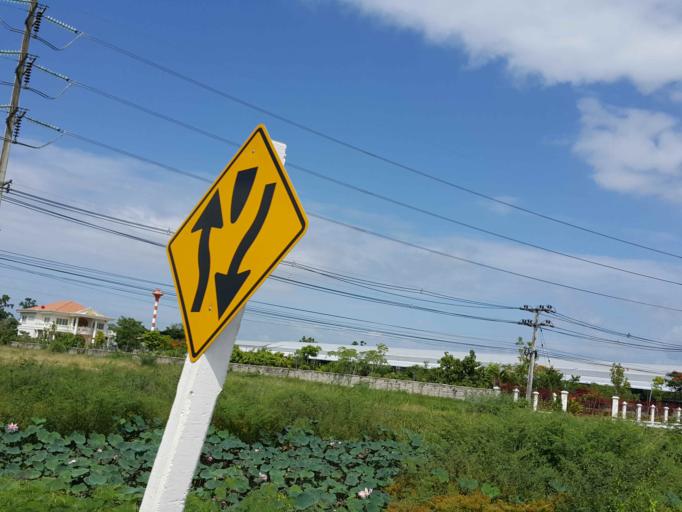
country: TH
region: Chiang Mai
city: San Kamphaeng
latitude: 18.7452
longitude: 99.0735
